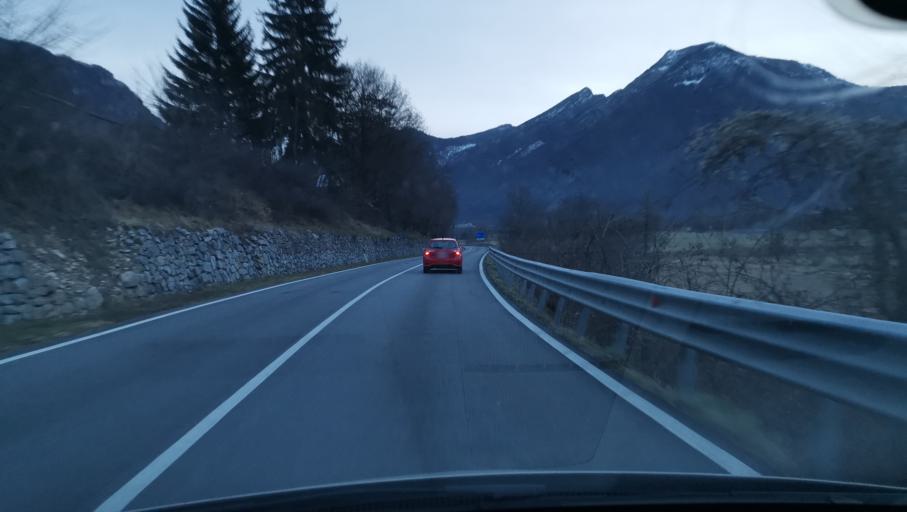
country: IT
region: Piedmont
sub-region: Provincia di Cuneo
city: Demonte
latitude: 44.3140
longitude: 7.3380
